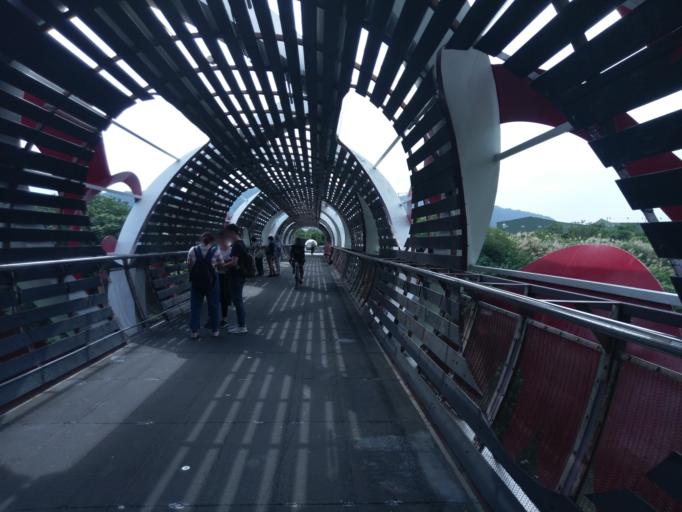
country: TW
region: Taiwan
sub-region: Taoyuan
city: Taoyuan
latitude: 24.9508
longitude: 121.3569
